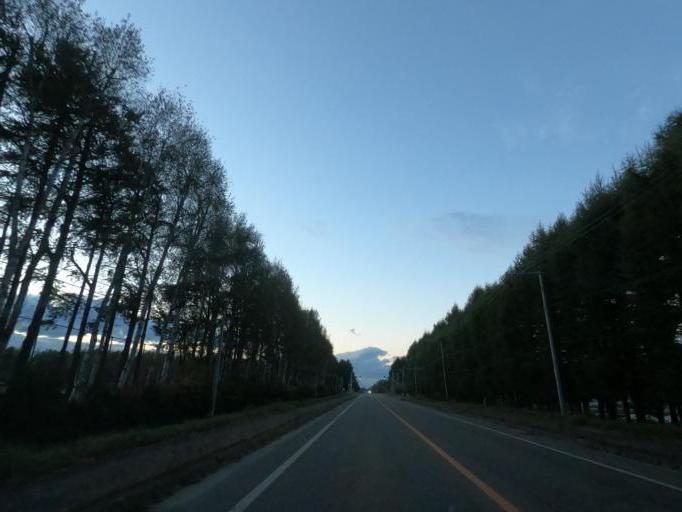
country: JP
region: Hokkaido
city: Obihiro
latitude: 42.6564
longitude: 143.1864
